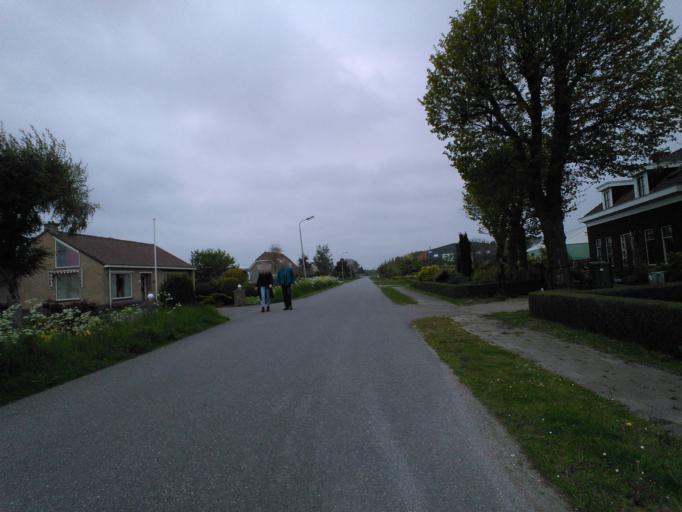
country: NL
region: South Holland
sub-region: Gemeente Pijnacker-Nootdorp
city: Pijnacker
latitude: 52.0483
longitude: 4.4271
